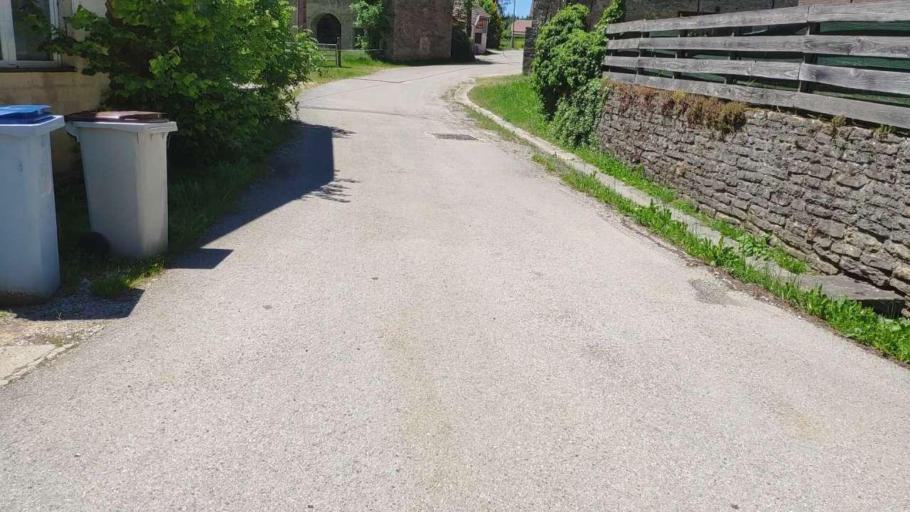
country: FR
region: Franche-Comte
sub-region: Departement du Jura
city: Poligny
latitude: 46.7659
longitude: 5.6853
